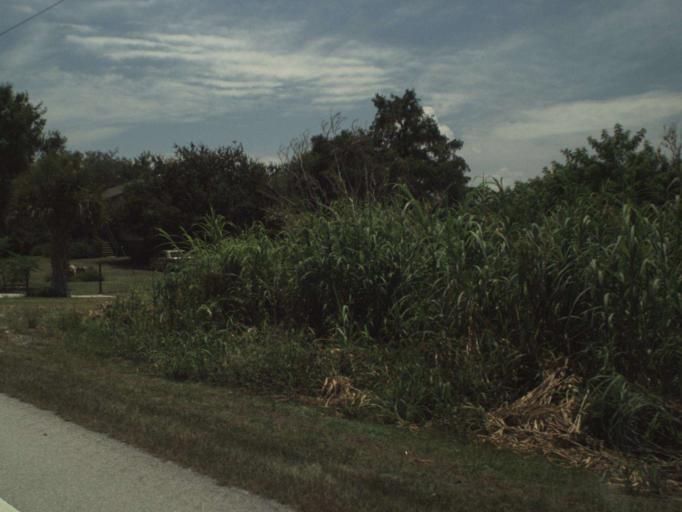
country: US
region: Florida
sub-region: Martin County
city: Indiantown
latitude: 27.0058
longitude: -80.6239
